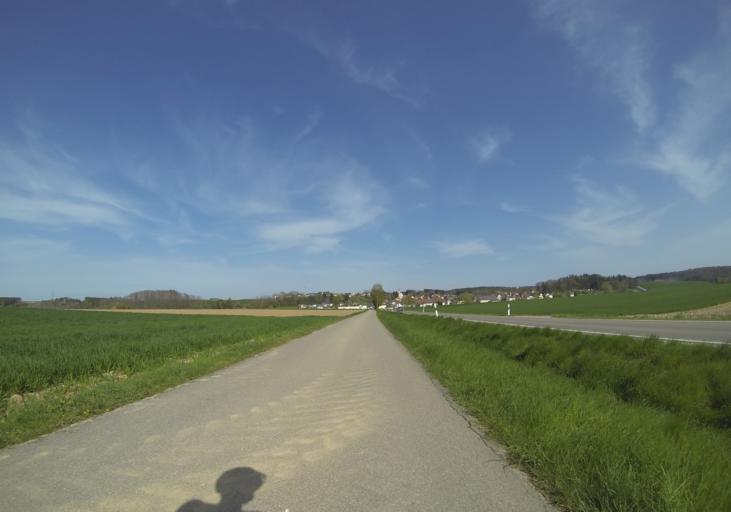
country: DE
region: Baden-Wuerttemberg
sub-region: Tuebingen Region
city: Huttisheim
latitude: 48.2613
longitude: 9.9455
